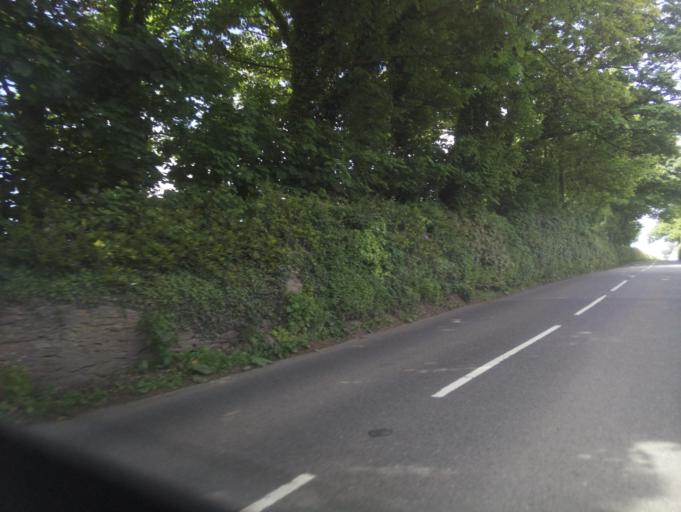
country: GB
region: England
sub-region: Devon
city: South Brent
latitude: 50.3928
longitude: -3.8443
